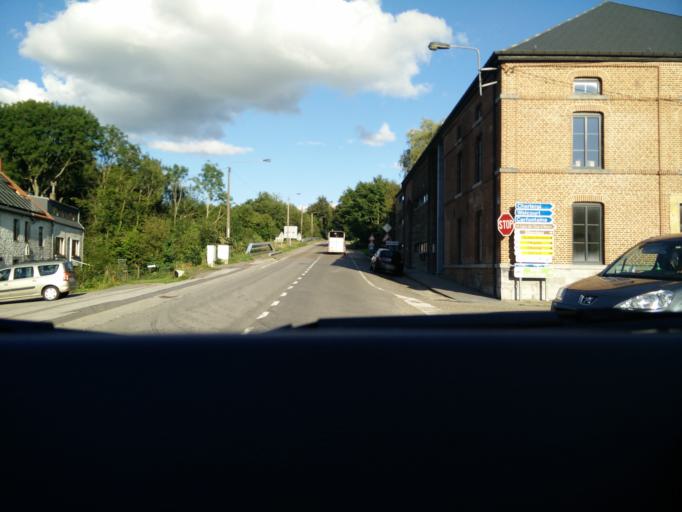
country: BE
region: Wallonia
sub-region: Province de Namur
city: Walcourt
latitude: 50.2245
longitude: 4.4127
